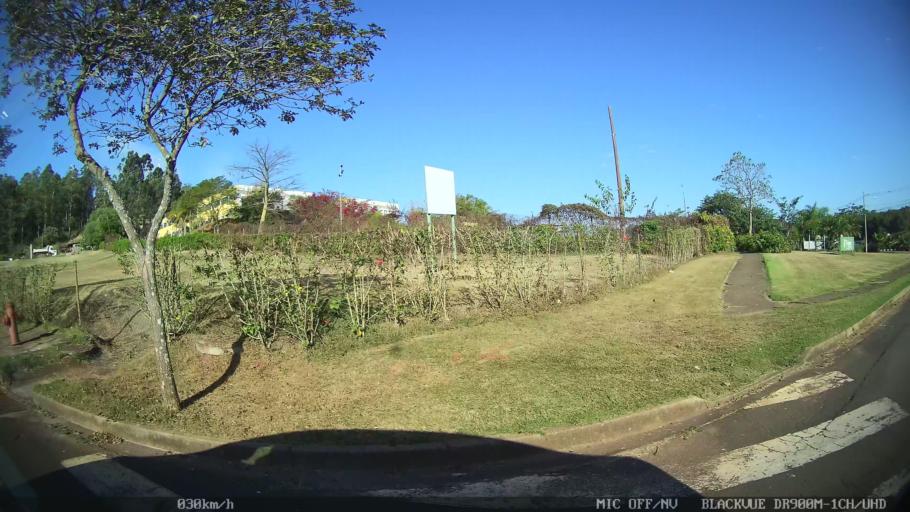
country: BR
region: Sao Paulo
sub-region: Piracicaba
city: Piracicaba
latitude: -22.6927
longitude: -47.6263
